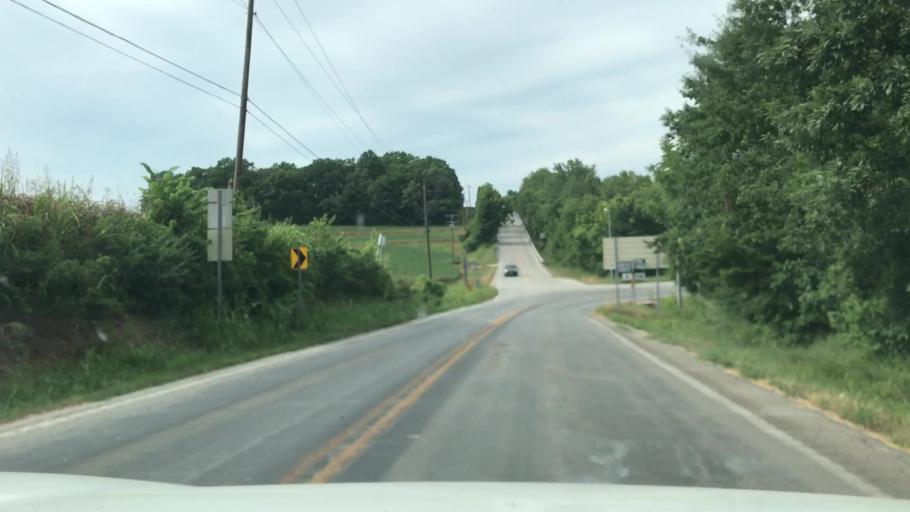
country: US
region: Missouri
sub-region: Saint Charles County
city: Weldon Spring
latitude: 38.6520
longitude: -90.7762
